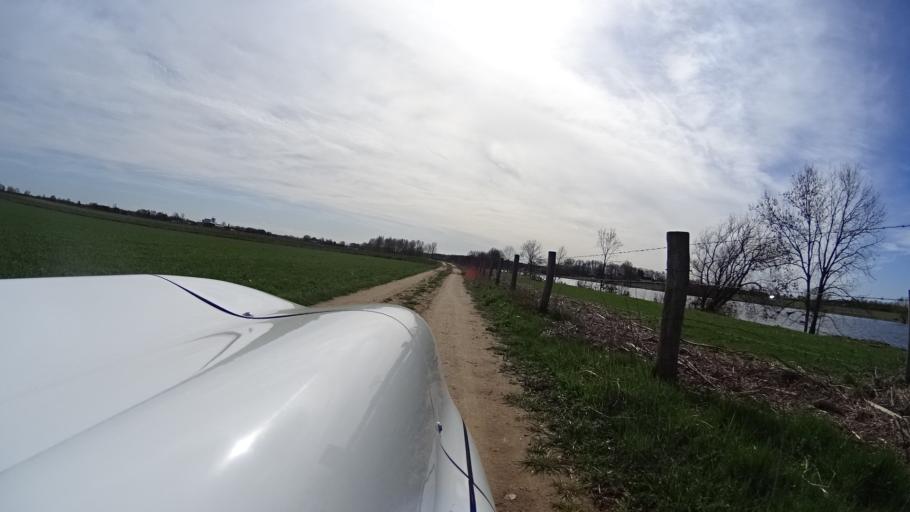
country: NL
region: Limburg
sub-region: Gemeente Venlo
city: Arcen
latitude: 51.4929
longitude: 6.1689
